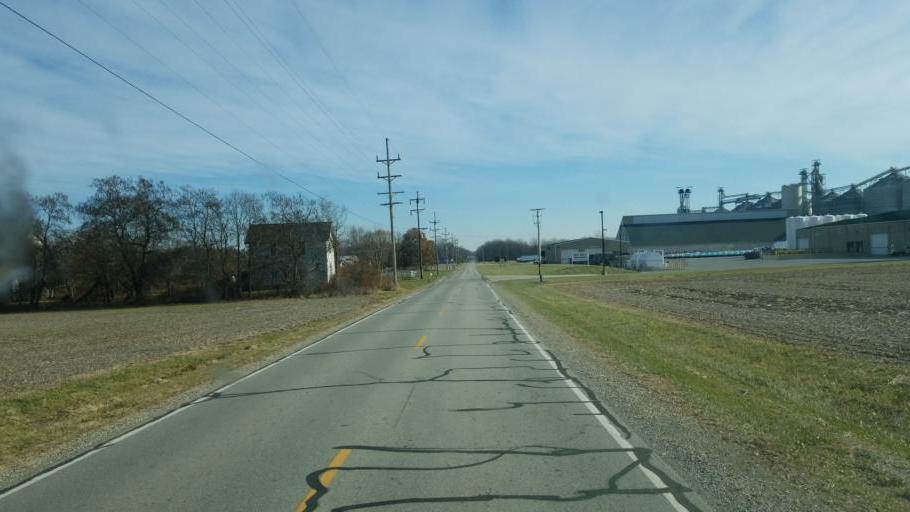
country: US
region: Ohio
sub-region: Crawford County
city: Crestline
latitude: 40.7852
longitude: -82.7861
